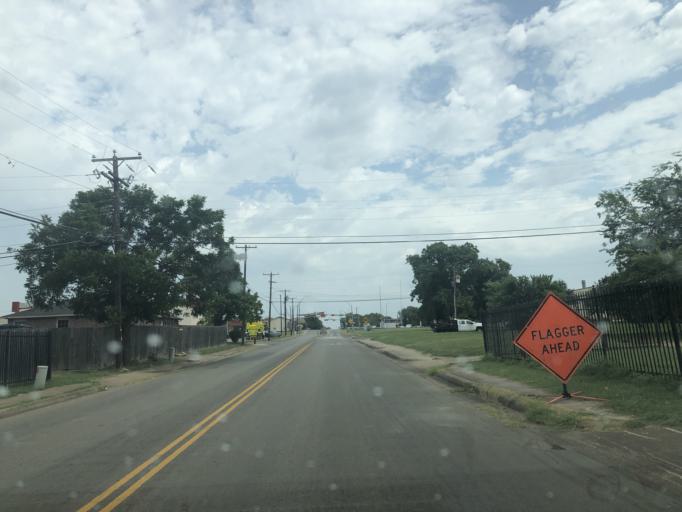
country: US
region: Texas
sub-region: Dallas County
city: Grand Prairie
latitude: 32.7382
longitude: -97.0291
